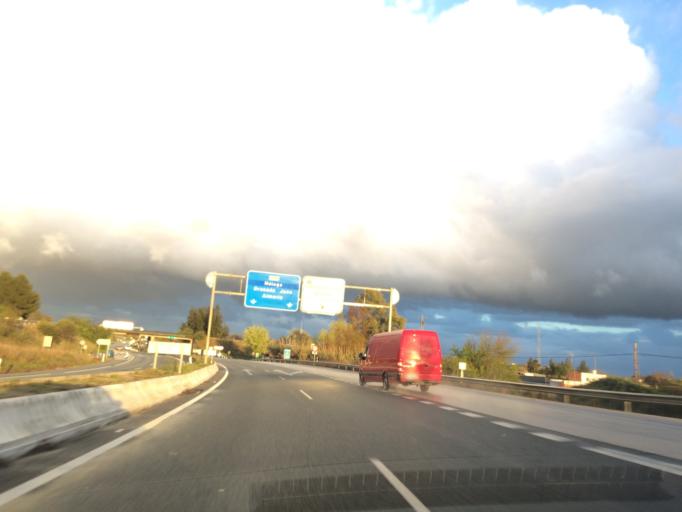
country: ES
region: Andalusia
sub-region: Provincia de Sevilla
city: Alcala de Guadaira
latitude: 37.3282
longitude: -5.8177
